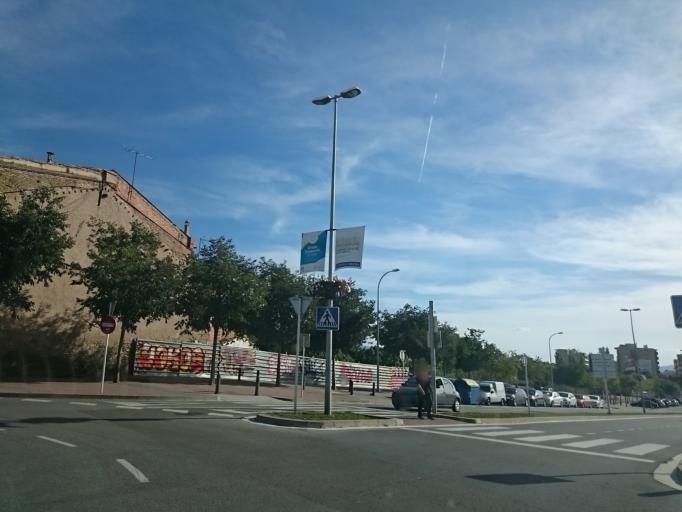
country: ES
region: Catalonia
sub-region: Provincia de Barcelona
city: Vic
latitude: 41.9289
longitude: 2.2609
